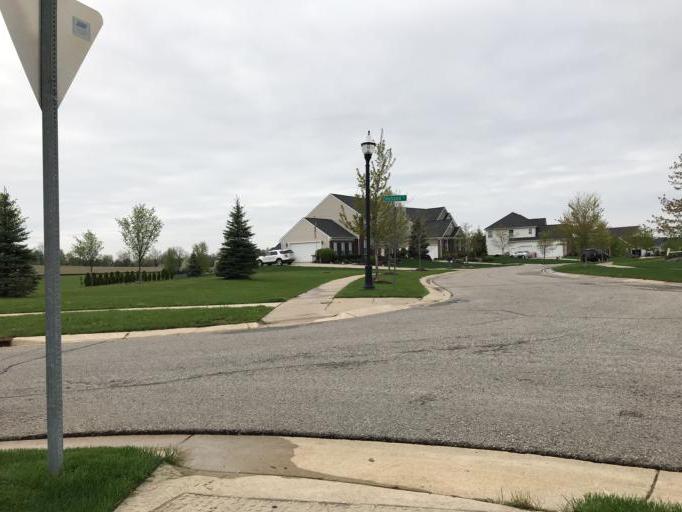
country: US
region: Michigan
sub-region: Oakland County
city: South Lyon
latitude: 42.4778
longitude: -83.6251
